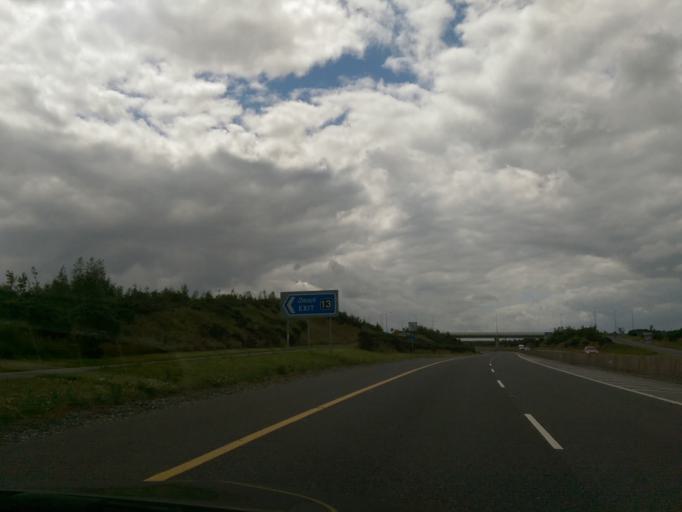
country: IE
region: Munster
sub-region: County Cork
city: Mitchelstown
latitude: 52.2401
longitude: -8.2754
